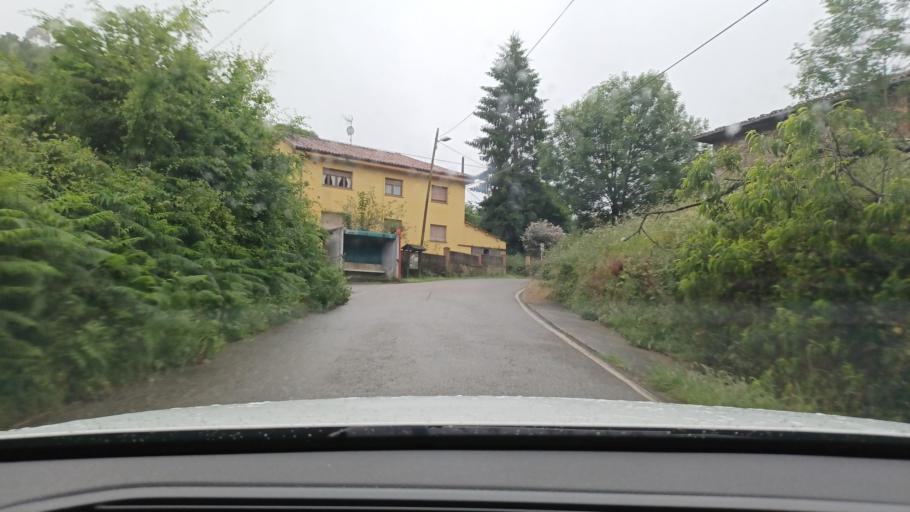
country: ES
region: Asturias
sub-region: Province of Asturias
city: Castandiello
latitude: 43.3027
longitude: -5.9347
